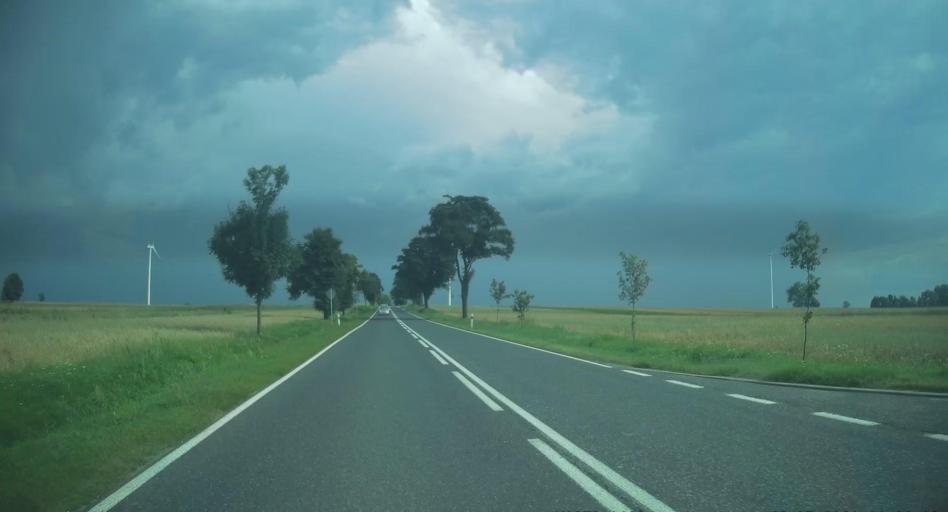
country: PL
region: Lodz Voivodeship
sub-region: Powiat skierniewicki
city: Gluchow
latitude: 51.7974
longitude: 20.0288
